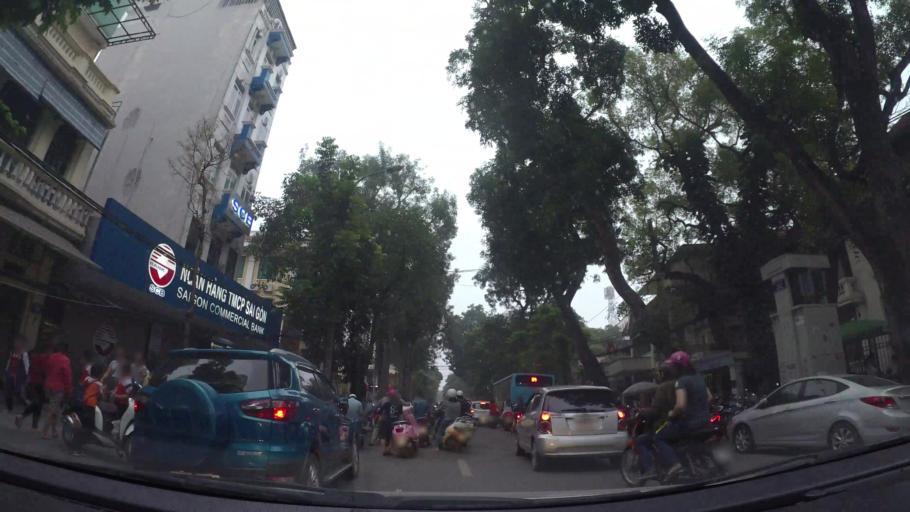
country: VN
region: Ha Noi
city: Hoan Kiem
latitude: 21.0308
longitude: 105.8550
